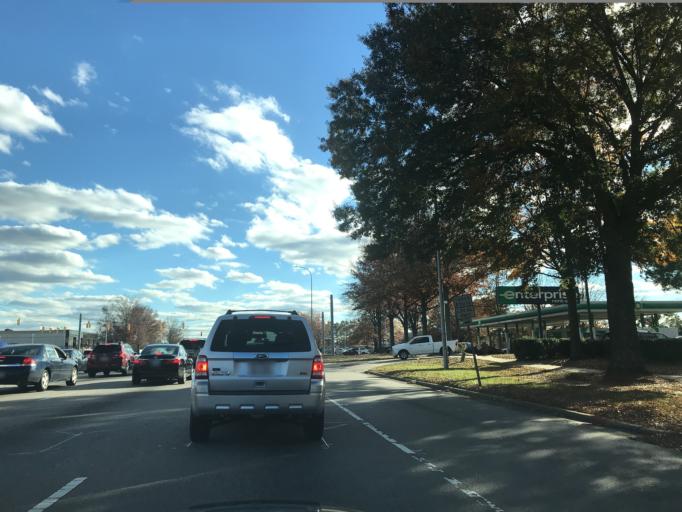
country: US
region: North Carolina
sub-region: Wake County
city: Raleigh
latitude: 35.8562
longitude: -78.5814
